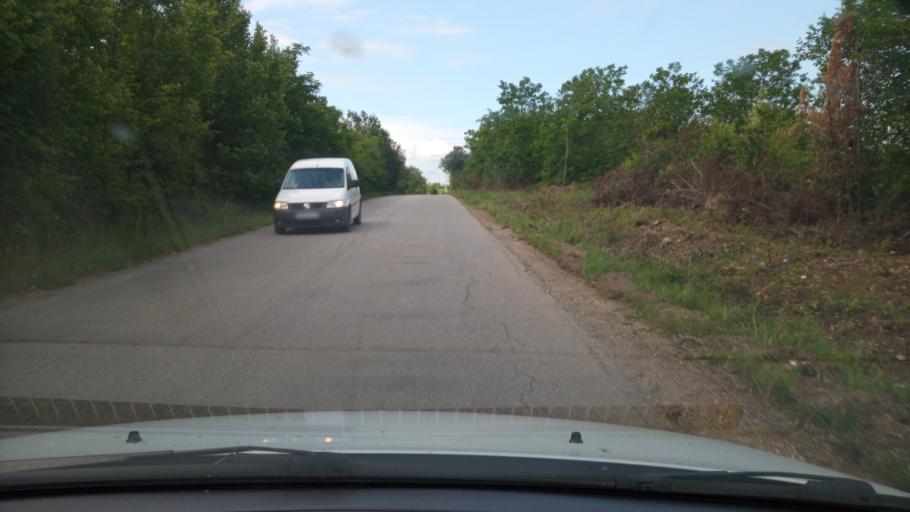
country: BG
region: Lovech
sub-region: Obshtina Lukovit
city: Lukovit
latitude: 43.1998
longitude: 24.1194
